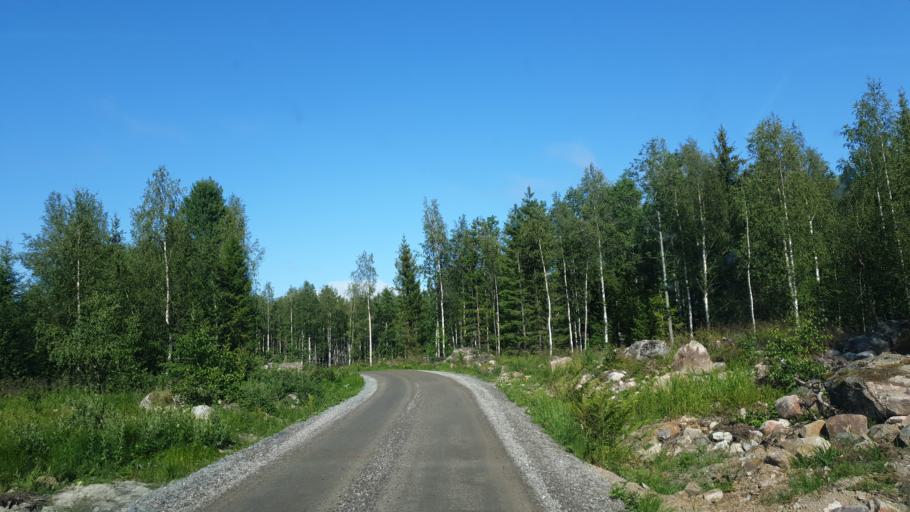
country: SE
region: Gaevleborg
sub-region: Soderhamns Kommun
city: Marielund
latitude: 61.4522
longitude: 17.0653
